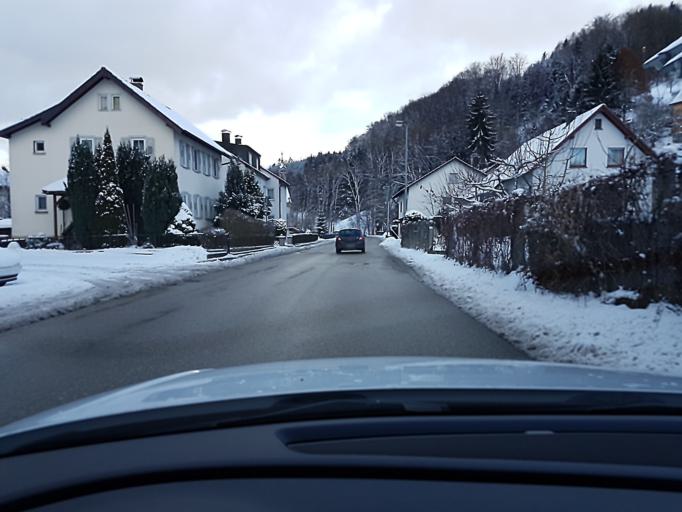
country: DE
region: Baden-Wuerttemberg
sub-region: Regierungsbezirk Stuttgart
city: Spiegelberg
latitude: 49.0595
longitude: 9.4331
